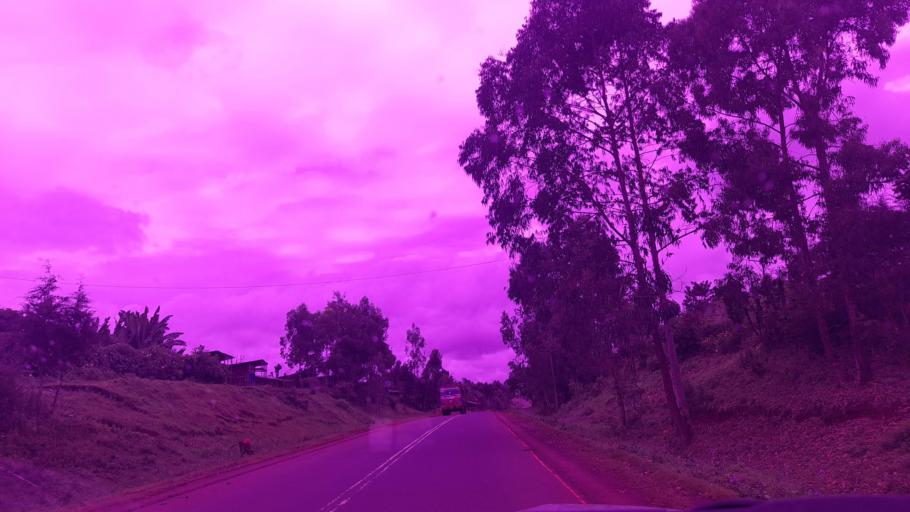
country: ET
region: Southern Nations, Nationalities, and People's Region
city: Bonga
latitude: 7.3011
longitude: 35.9921
